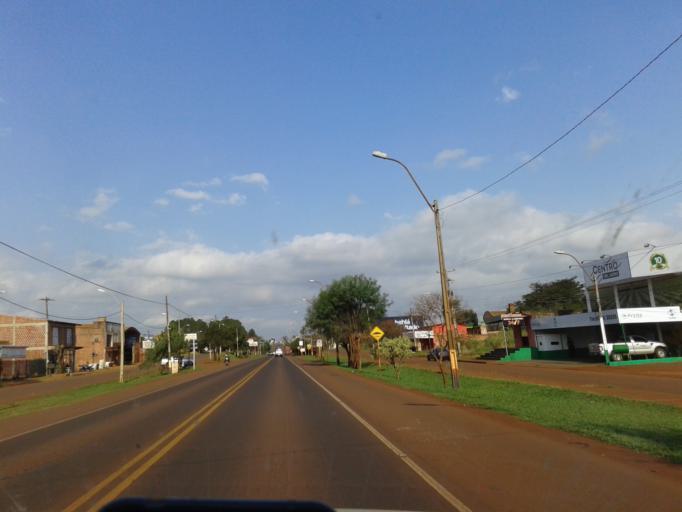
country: PY
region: Itapua
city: Arquitecto Tomas Romero Pereira
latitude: -26.5182
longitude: -55.2696
